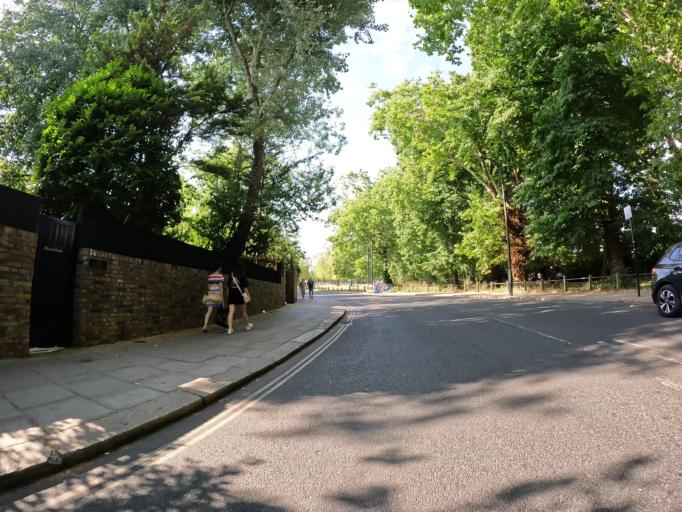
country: GB
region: England
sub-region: Greater London
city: Hadley Wood
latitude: 51.6552
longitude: -0.1771
